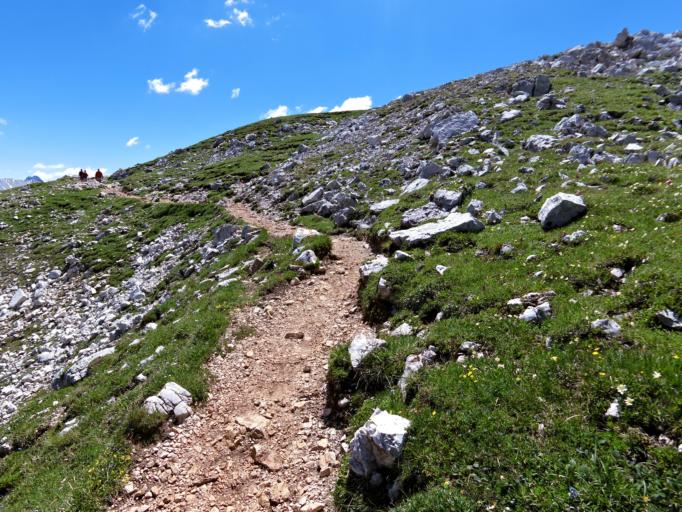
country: IT
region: Trentino-Alto Adige
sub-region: Bolzano
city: Siusi
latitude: 46.5033
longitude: 11.5978
